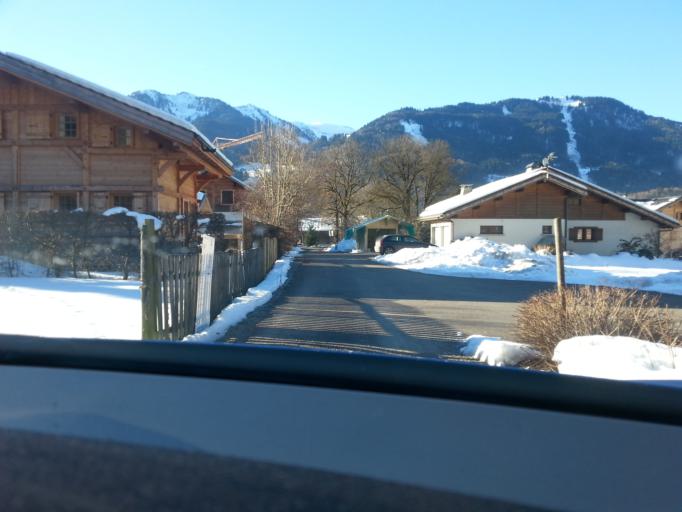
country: FR
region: Rhone-Alpes
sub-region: Departement de la Haute-Savoie
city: Samoens
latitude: 46.0842
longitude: 6.7311
